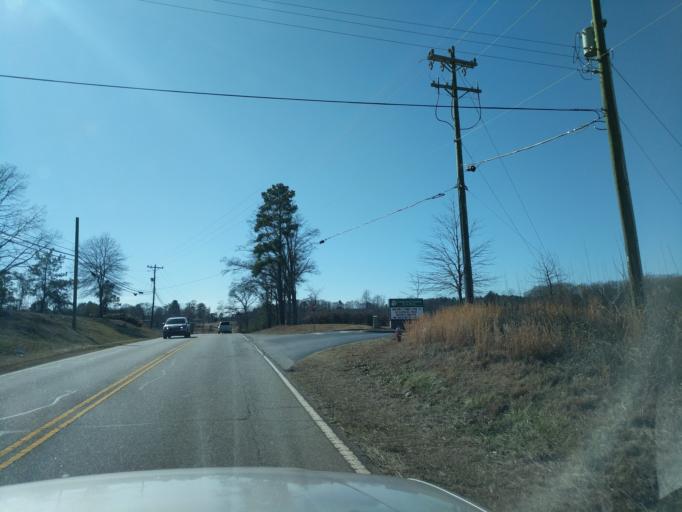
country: US
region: South Carolina
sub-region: Anderson County
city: Homeland Park
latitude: 34.4789
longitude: -82.6659
